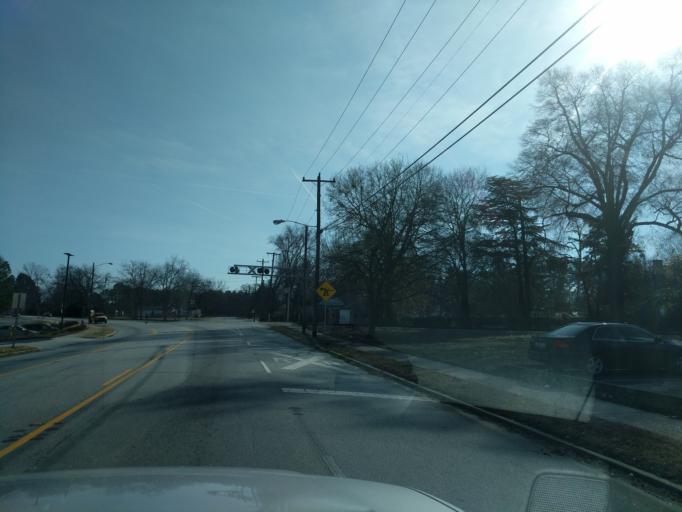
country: US
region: South Carolina
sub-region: Spartanburg County
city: Woodruff
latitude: 34.7371
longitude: -82.0355
